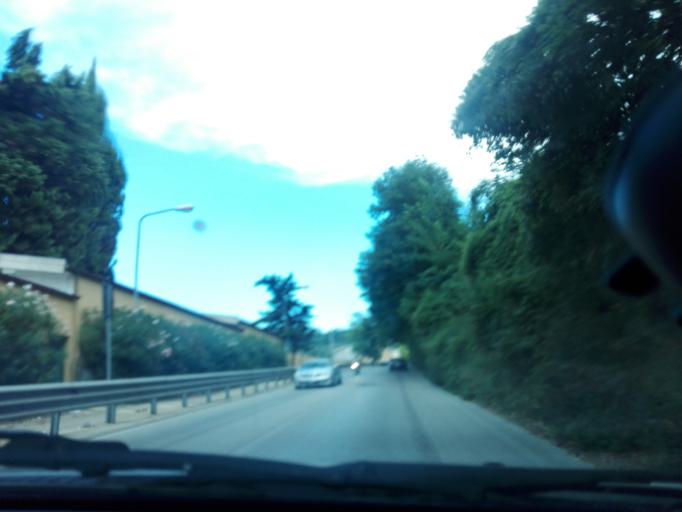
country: IT
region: Abruzzo
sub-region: Provincia di Pescara
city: Montesilvano Marina
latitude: 42.5005
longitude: 14.1396
